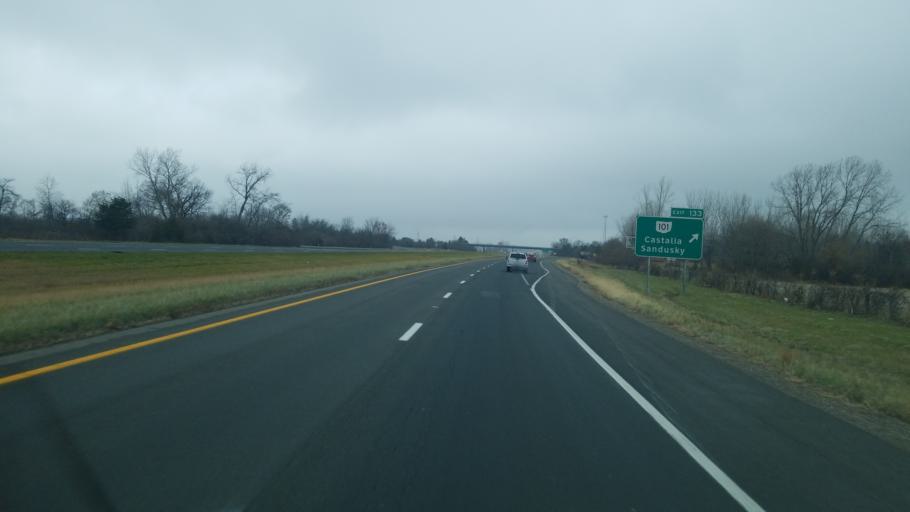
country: US
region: Ohio
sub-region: Erie County
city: Sandusky
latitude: 41.4144
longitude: -82.7542
